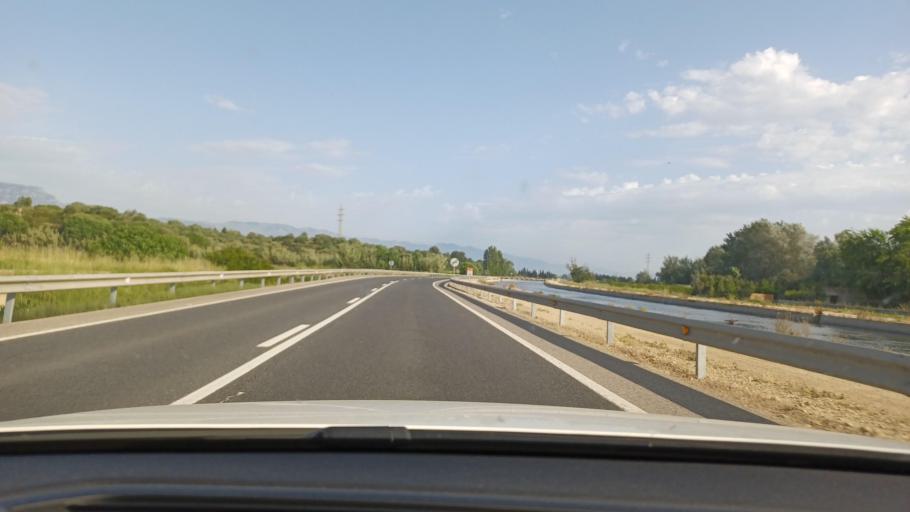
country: ES
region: Catalonia
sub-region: Provincia de Tarragona
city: Masdenverge
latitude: 40.7586
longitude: 0.5363
